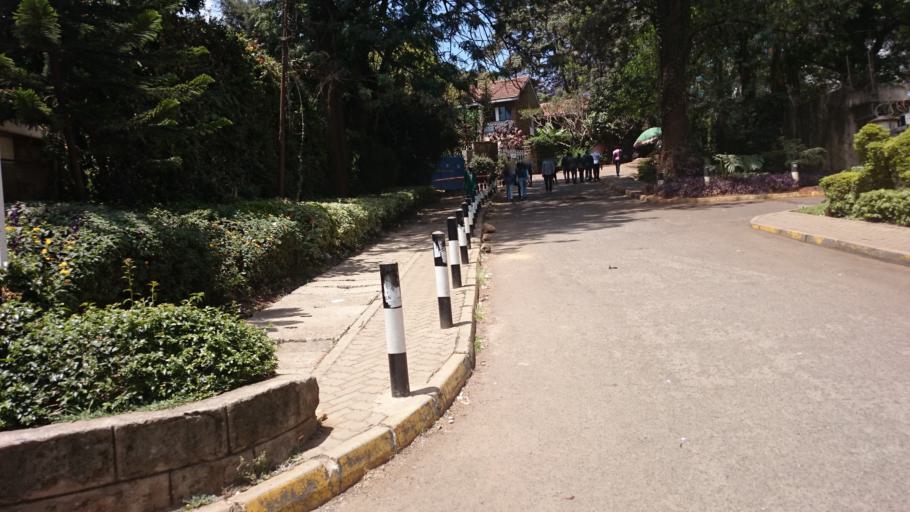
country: KE
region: Nairobi Area
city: Nairobi
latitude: -1.2820
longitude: 36.8137
